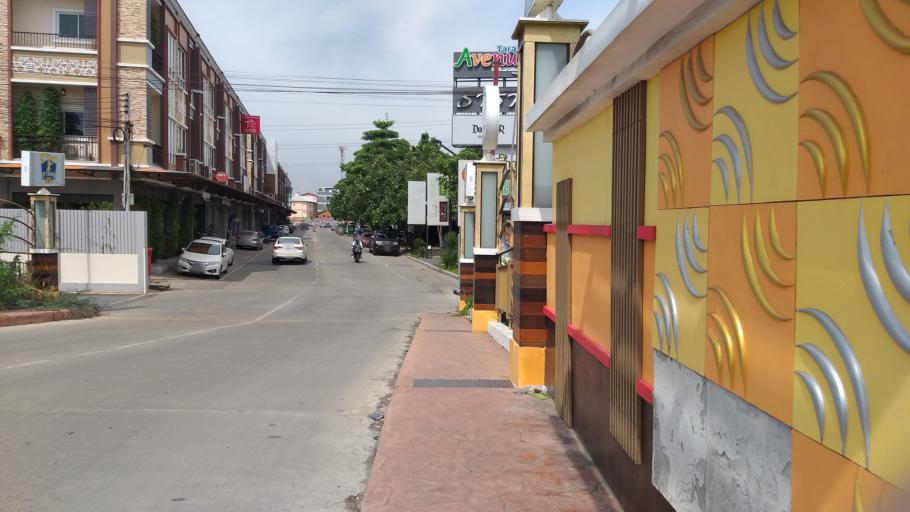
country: TH
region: Pathum Thani
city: Khlong Luang
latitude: 13.9962
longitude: 100.6641
